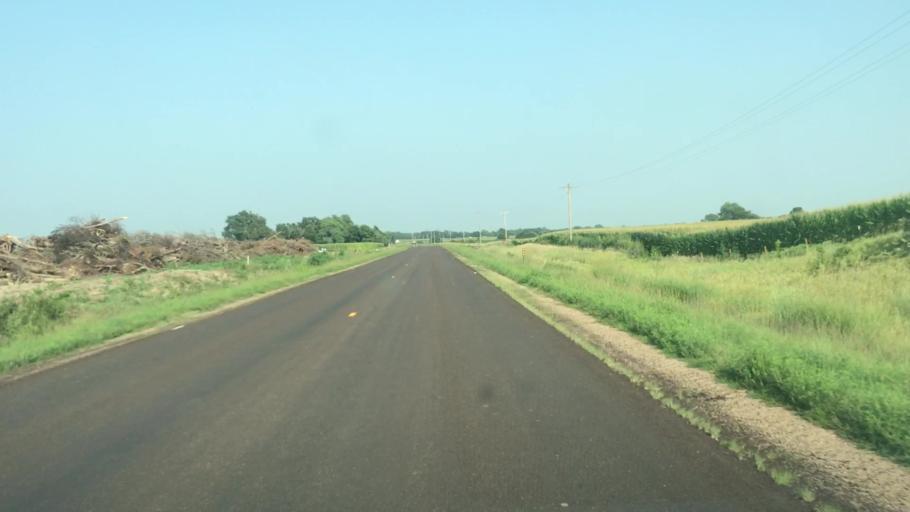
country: US
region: Nebraska
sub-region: Buffalo County
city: Ravenna
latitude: 41.0757
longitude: -98.7426
